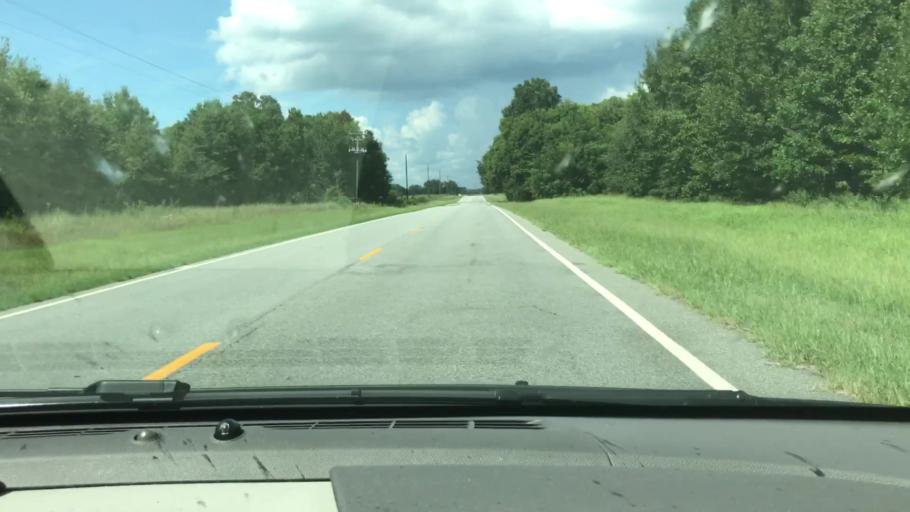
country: US
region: Georgia
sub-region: Quitman County
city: Georgetown
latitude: 31.7987
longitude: -85.0926
